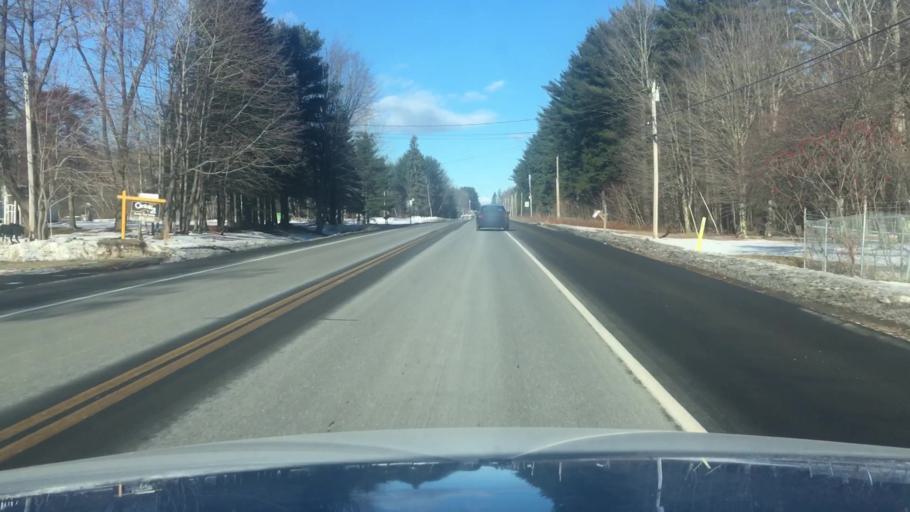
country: US
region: Maine
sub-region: Kennebec County
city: Waterville
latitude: 44.6128
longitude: -69.6666
